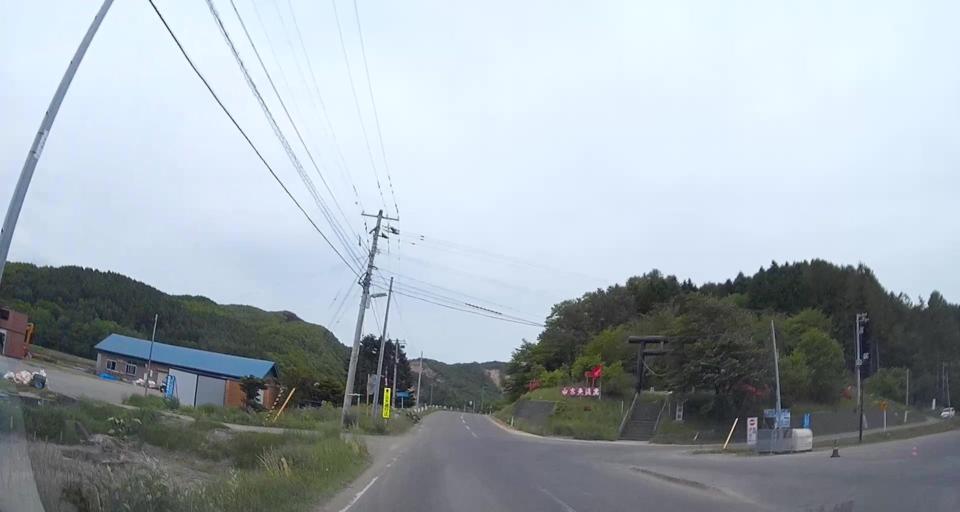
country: JP
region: Hokkaido
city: Chitose
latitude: 42.7557
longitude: 141.9779
